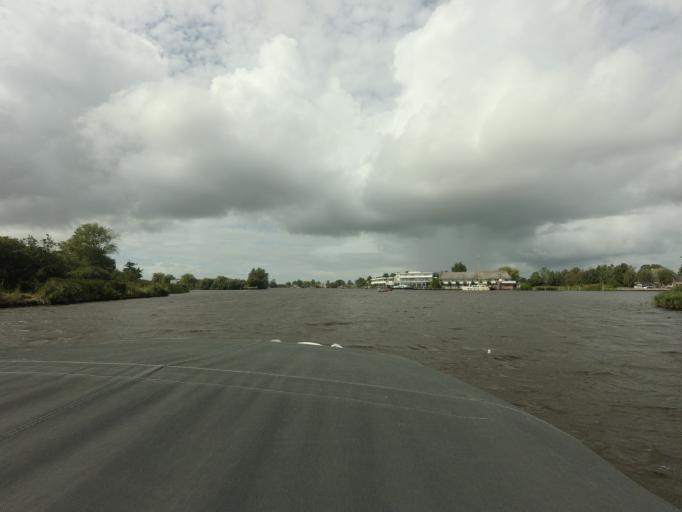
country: NL
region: Friesland
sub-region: Gemeente Boarnsterhim
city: Warten
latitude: 53.1267
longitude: 5.9356
